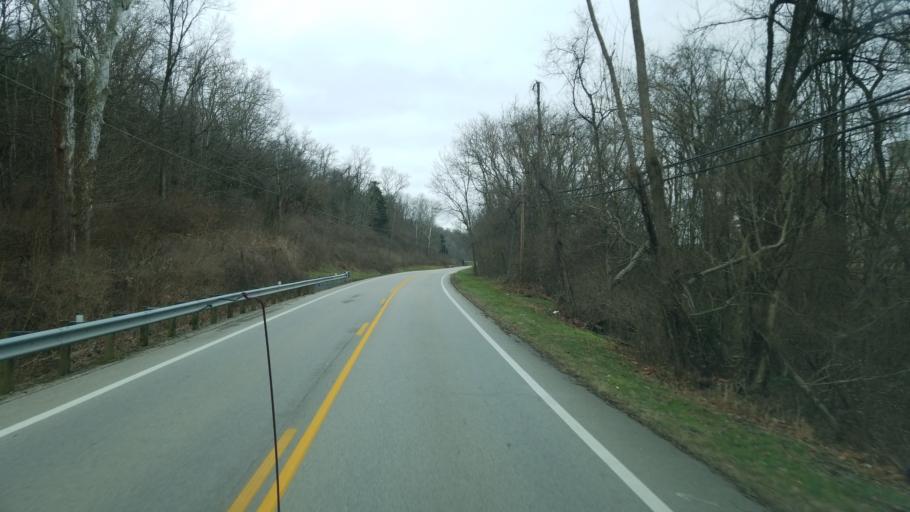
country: US
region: Ohio
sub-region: Clermont County
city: New Richmond
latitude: 38.8737
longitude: -84.2252
